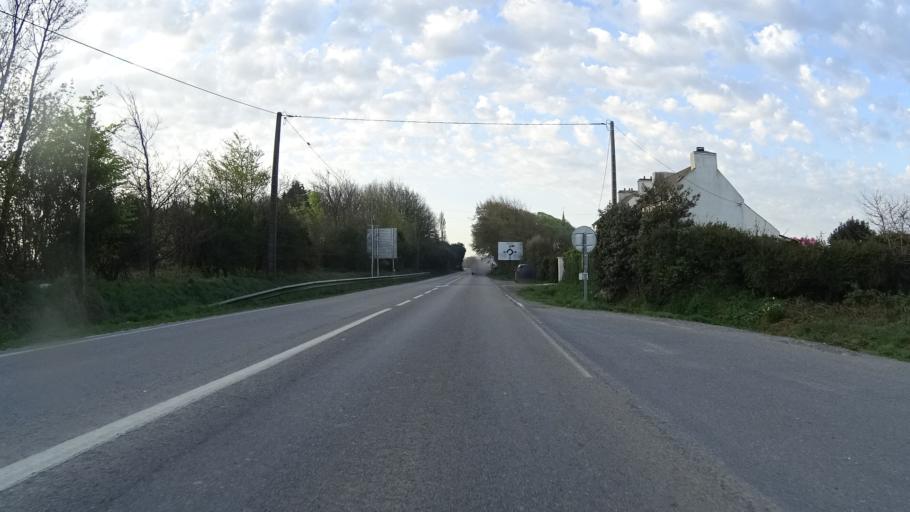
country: FR
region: Brittany
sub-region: Departement du Finistere
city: Plouedern
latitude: 48.4816
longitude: -4.2897
